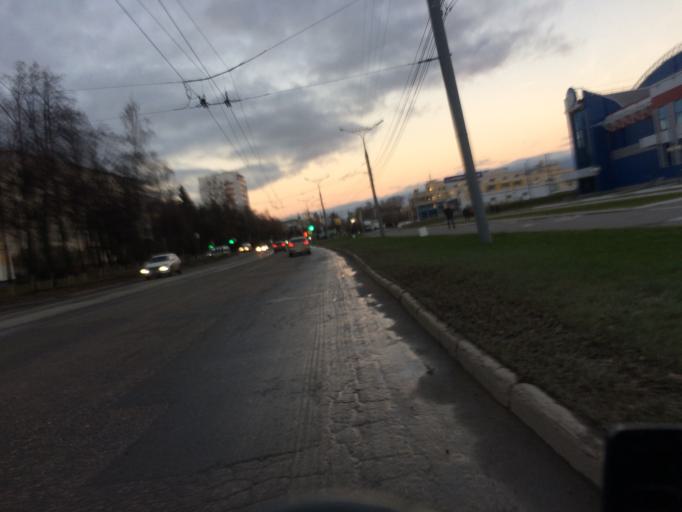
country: RU
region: Mariy-El
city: Yoshkar-Ola
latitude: 56.6262
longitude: 47.8942
